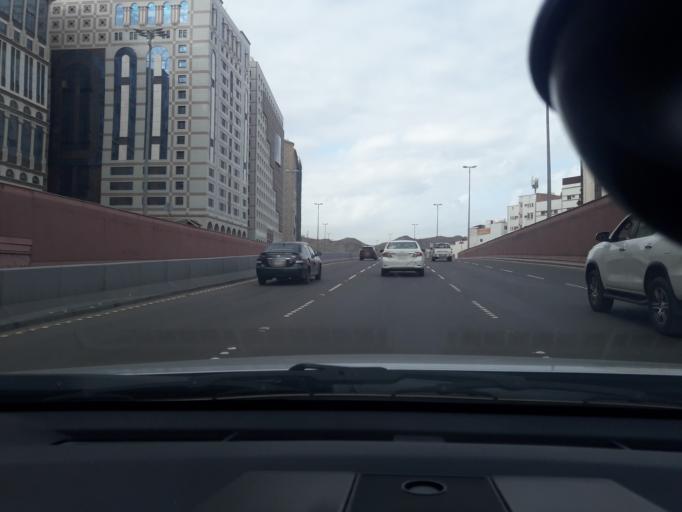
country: SA
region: Al Madinah al Munawwarah
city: Medina
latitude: 24.4743
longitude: 39.6095
